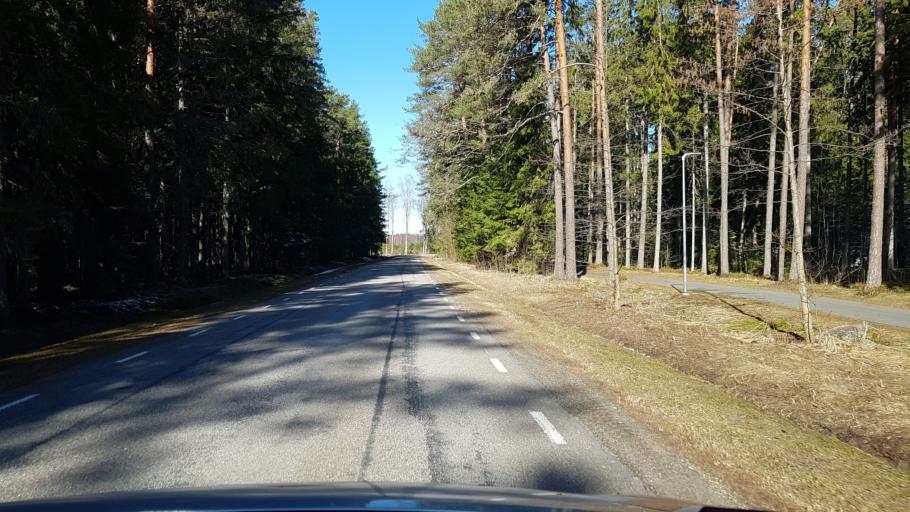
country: EE
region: Harju
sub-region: Loksa linn
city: Loksa
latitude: 59.5771
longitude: 25.9231
